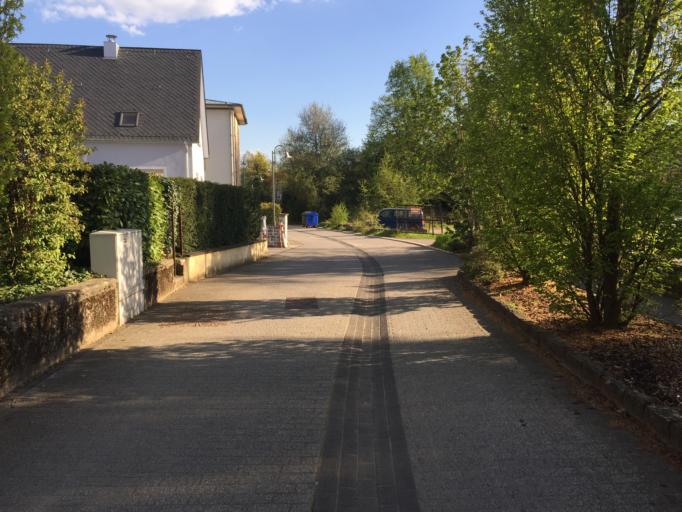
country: LU
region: Luxembourg
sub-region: Canton de Capellen
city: Steinfort
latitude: 49.6593
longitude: 5.9150
